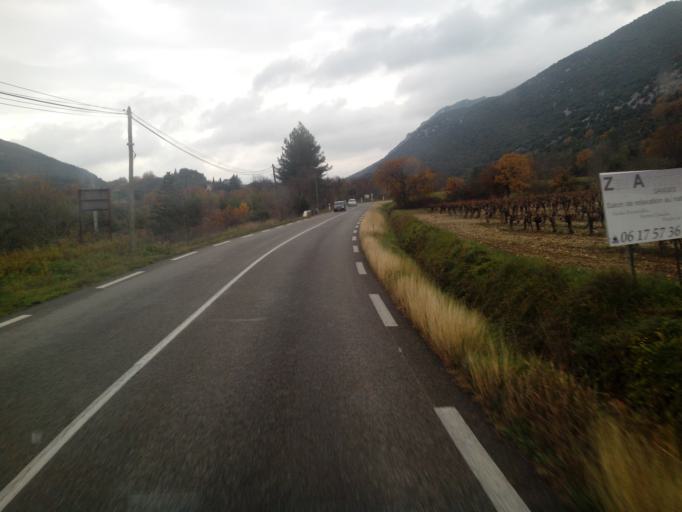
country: FR
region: Languedoc-Roussillon
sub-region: Departement du Gard
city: Saint-Hippolyte-du-Fort
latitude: 43.9581
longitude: 3.8349
